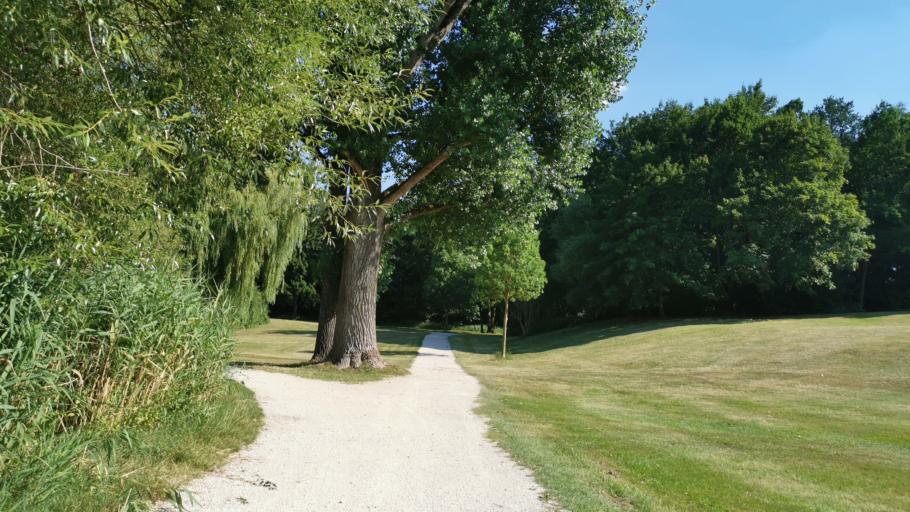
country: DE
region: Bavaria
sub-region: Regierungsbezirk Mittelfranken
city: Nuernberg
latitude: 49.4202
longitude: 11.1088
